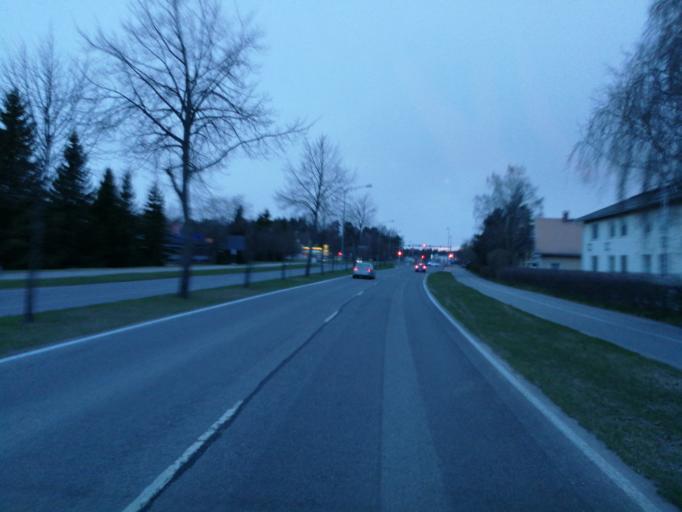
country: FI
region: Varsinais-Suomi
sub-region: Turku
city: Turku
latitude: 60.4690
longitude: 22.2389
